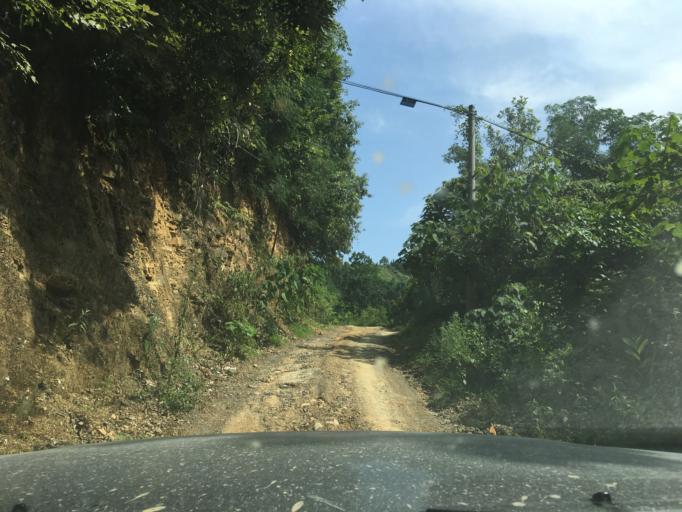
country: CN
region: Guangxi Zhuangzu Zizhiqu
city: Xinzhou
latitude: 25.0456
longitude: 105.8614
